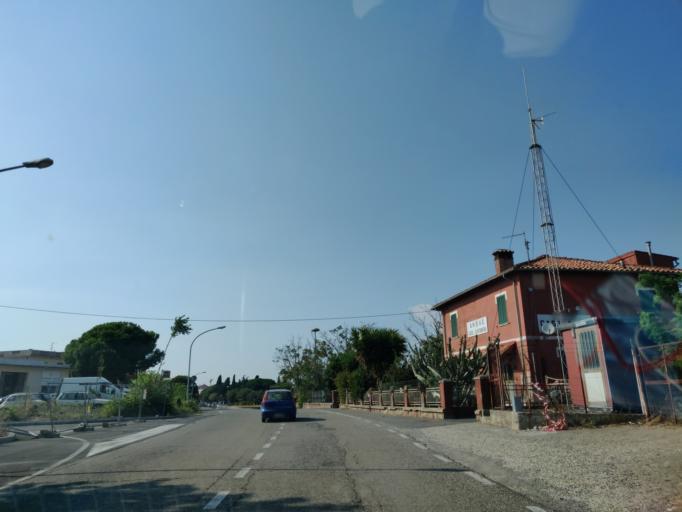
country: IT
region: Latium
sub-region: Provincia di Viterbo
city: Montalto di Castro
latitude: 42.3472
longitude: 11.6132
